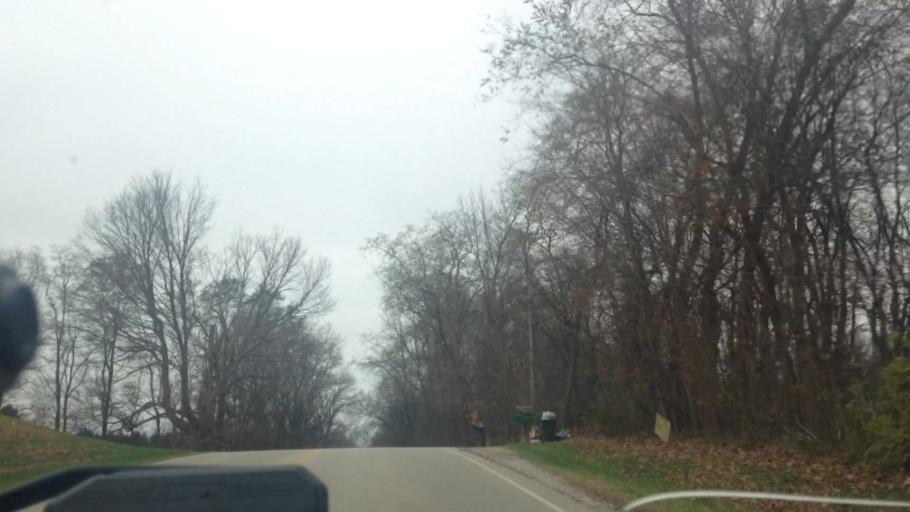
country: US
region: Wisconsin
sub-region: Waukesha County
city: Lannon
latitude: 43.1884
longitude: -88.1826
